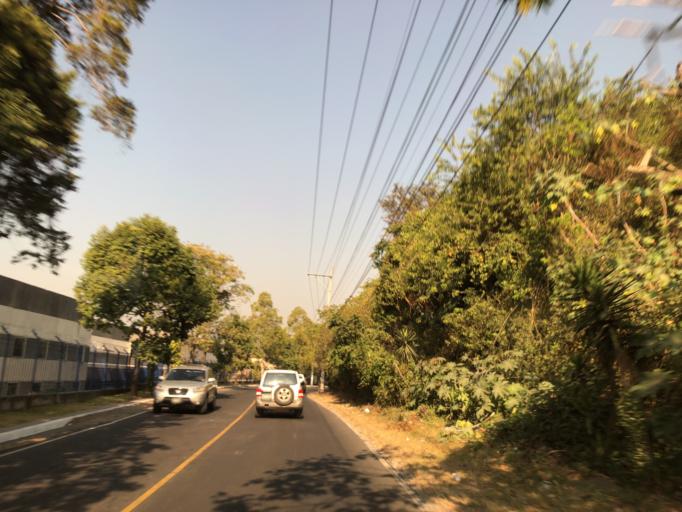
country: GT
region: Guatemala
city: Villa Canales
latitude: 14.4921
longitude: -90.5369
